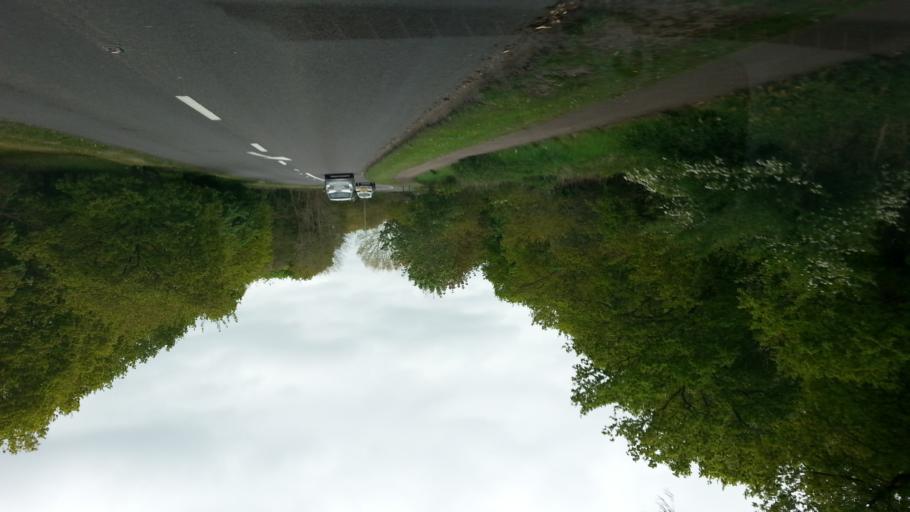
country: GB
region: England
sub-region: Suffolk
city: Lakenheath
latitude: 52.3401
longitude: 0.5301
